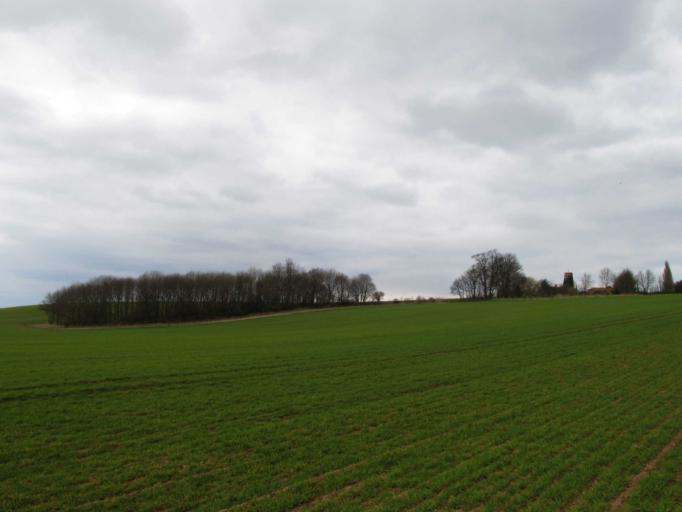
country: GB
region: England
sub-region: Nottinghamshire
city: Misterton
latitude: 53.4044
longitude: -0.9013
